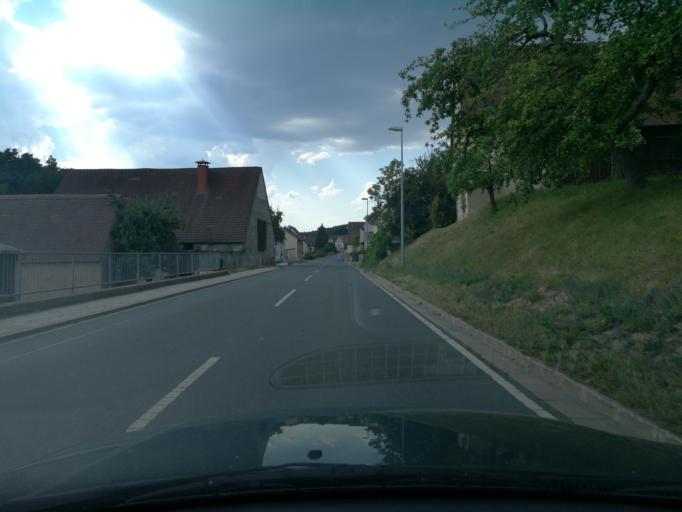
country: DE
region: Bavaria
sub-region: Regierungsbezirk Mittelfranken
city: Grosshabersdorf
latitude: 49.4079
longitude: 10.7680
